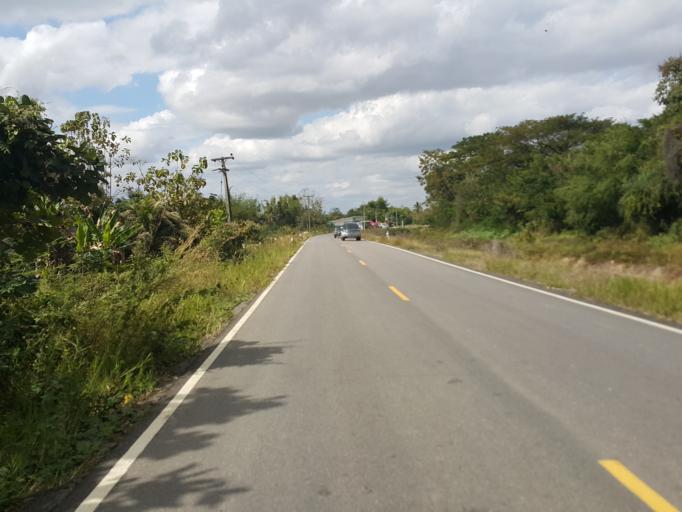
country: TH
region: Chiang Mai
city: San Kamphaeng
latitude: 18.8307
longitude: 99.1640
